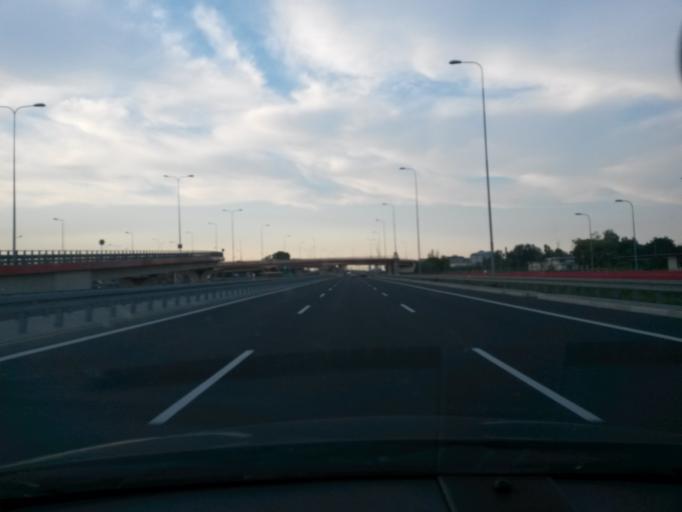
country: PL
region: Masovian Voivodeship
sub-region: Warszawa
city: Wlochy
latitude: 52.1657
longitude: 20.9864
